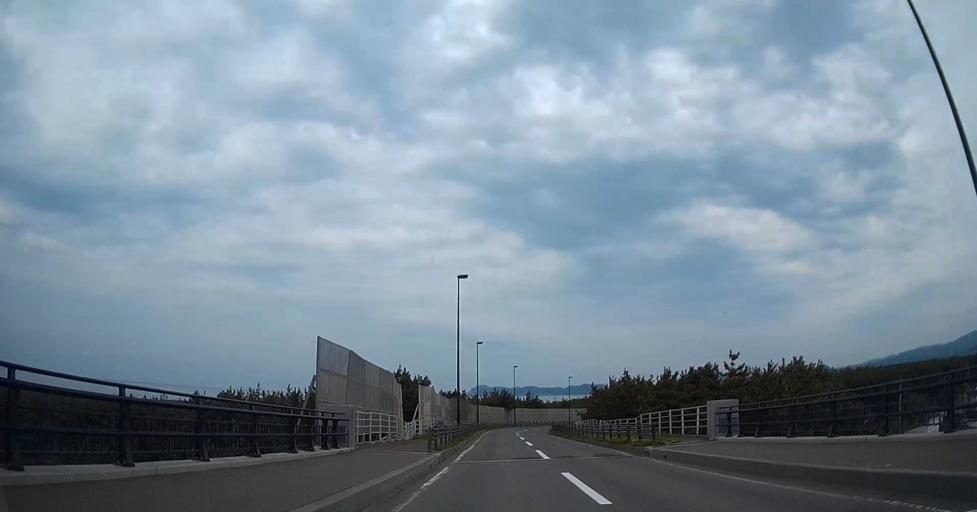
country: JP
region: Aomori
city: Shimokizukuri
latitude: 41.0394
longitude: 140.3260
